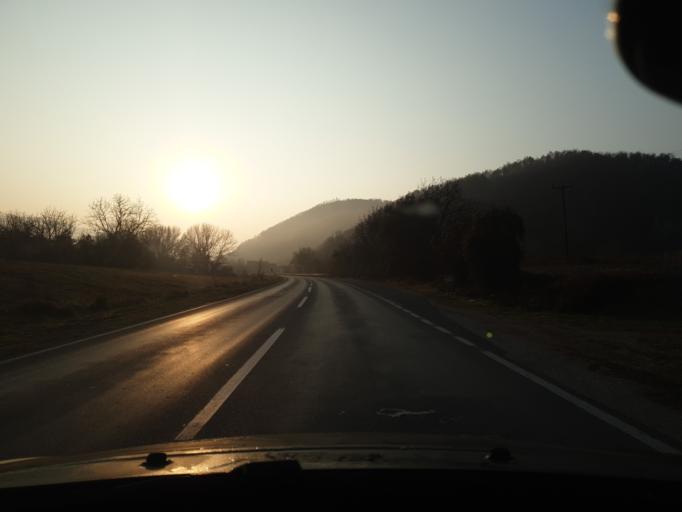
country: RS
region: Central Serbia
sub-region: Jablanicki Okrug
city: Vlasotince
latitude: 42.8981
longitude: 22.0464
